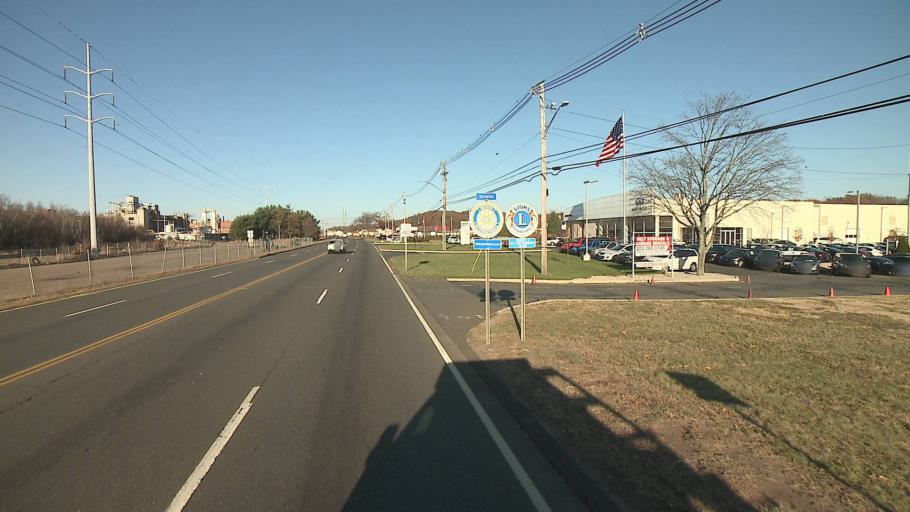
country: US
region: Connecticut
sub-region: New Haven County
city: Wallingford Center
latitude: 41.4309
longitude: -72.8360
